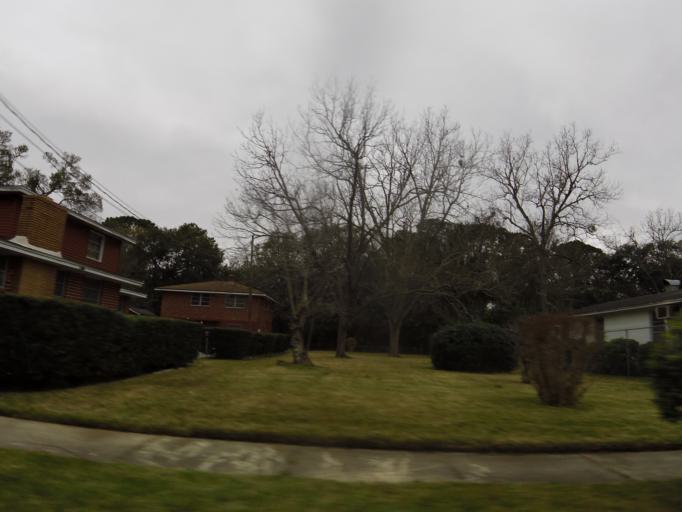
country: US
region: Florida
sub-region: Duval County
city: Jacksonville
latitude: 30.3552
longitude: -81.6837
